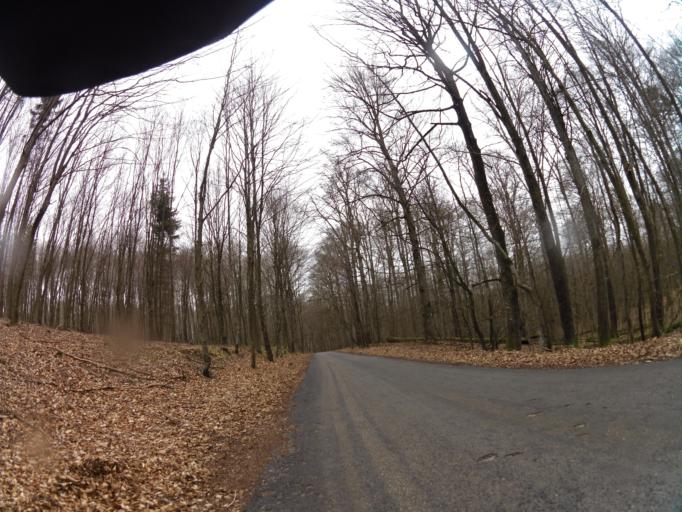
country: PL
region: West Pomeranian Voivodeship
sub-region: Powiat koszalinski
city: Bobolice
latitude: 53.9500
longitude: 16.6706
